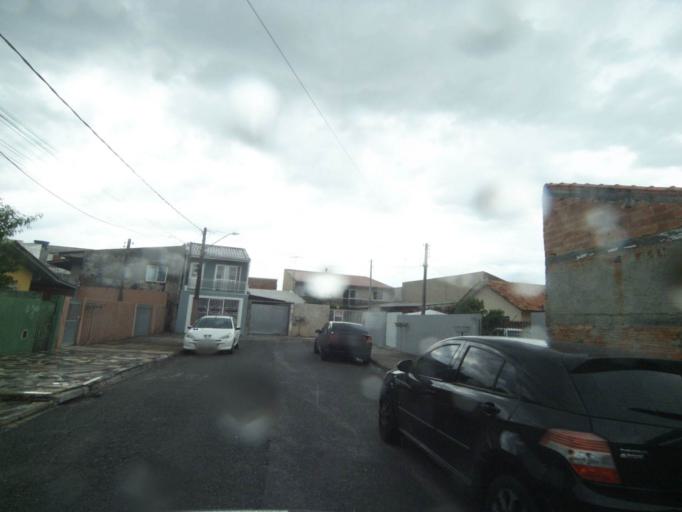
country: BR
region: Parana
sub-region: Pinhais
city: Pinhais
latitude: -25.4667
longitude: -49.1933
